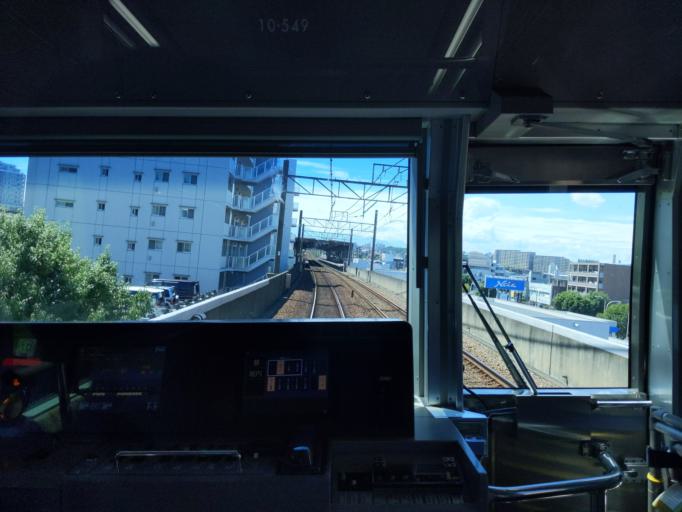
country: JP
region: Tokyo
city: Hino
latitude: 35.6256
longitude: 139.4027
